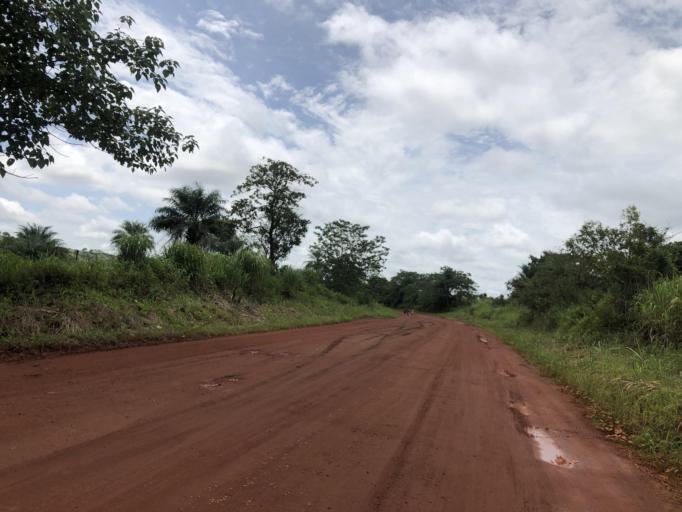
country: SL
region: Northern Province
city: Lunsar
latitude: 8.6701
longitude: -12.5284
